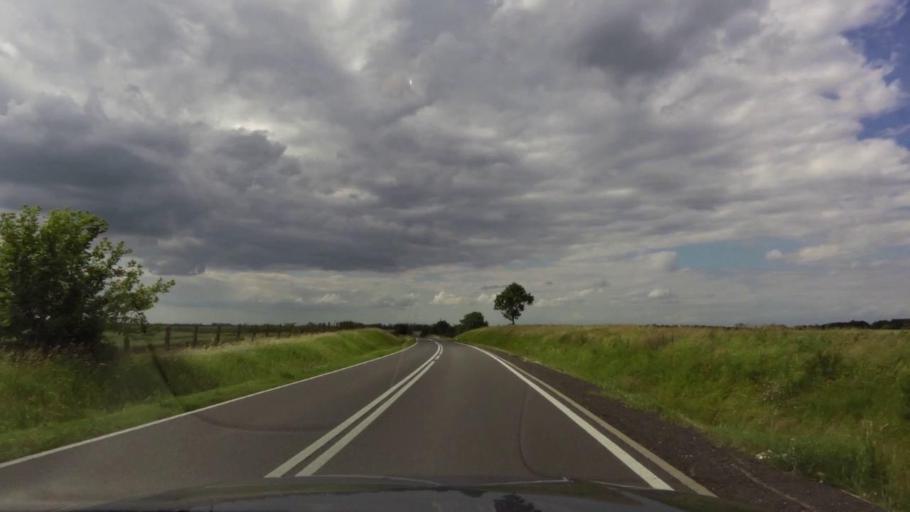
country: PL
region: West Pomeranian Voivodeship
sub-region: Powiat gryfinski
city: Mieszkowice
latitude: 52.8516
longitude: 14.4900
